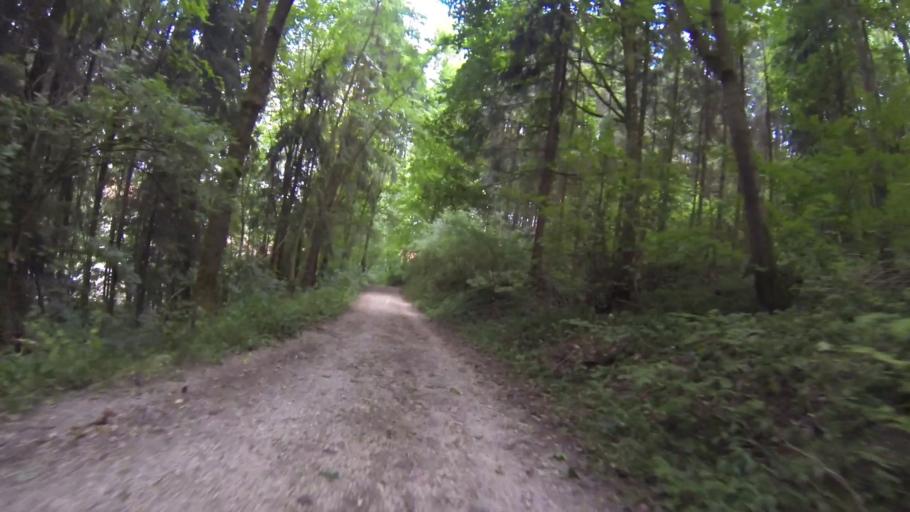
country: DE
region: Baden-Wuerttemberg
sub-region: Tuebingen Region
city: Dornstadt
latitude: 48.4309
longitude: 9.8851
